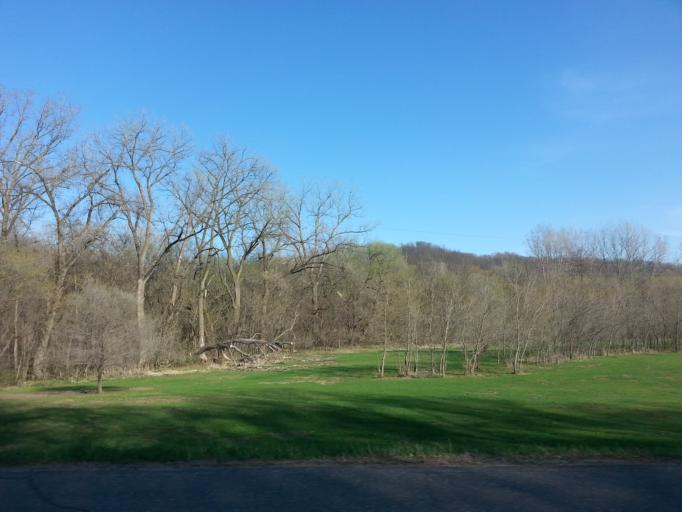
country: US
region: Wisconsin
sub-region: Pierce County
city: Ellsworth
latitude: 44.6767
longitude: -92.5896
